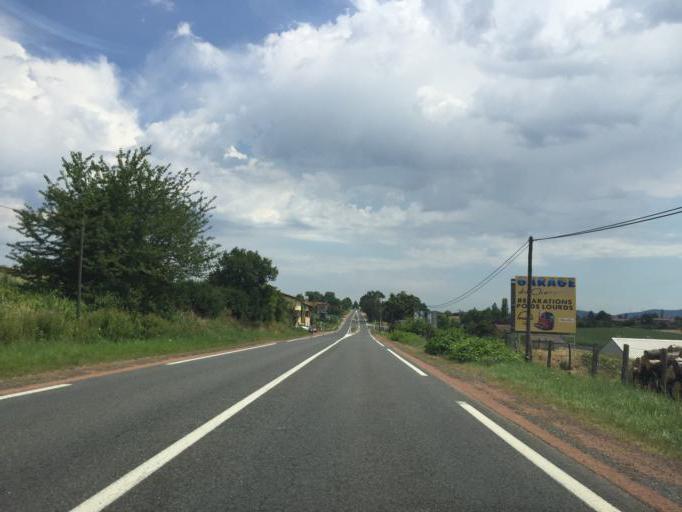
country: FR
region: Rhone-Alpes
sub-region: Departement du Rhone
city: Bully
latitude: 45.8600
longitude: 4.5613
